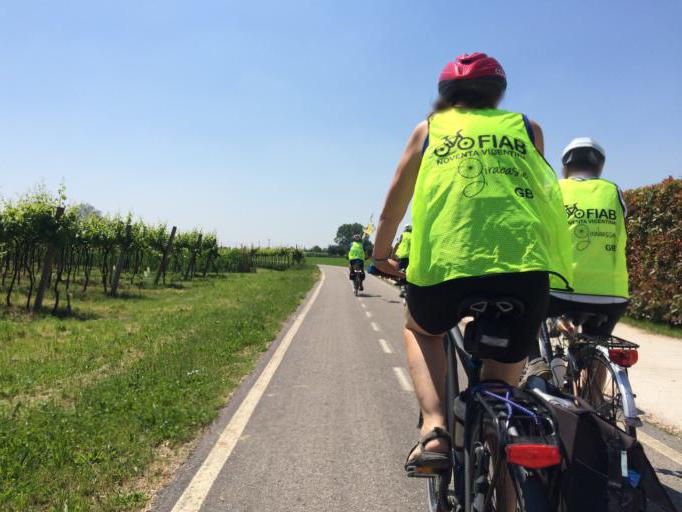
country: IT
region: Veneto
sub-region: Provincia di Vicenza
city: Ponte di Barbarano
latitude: 45.3935
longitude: 11.5630
